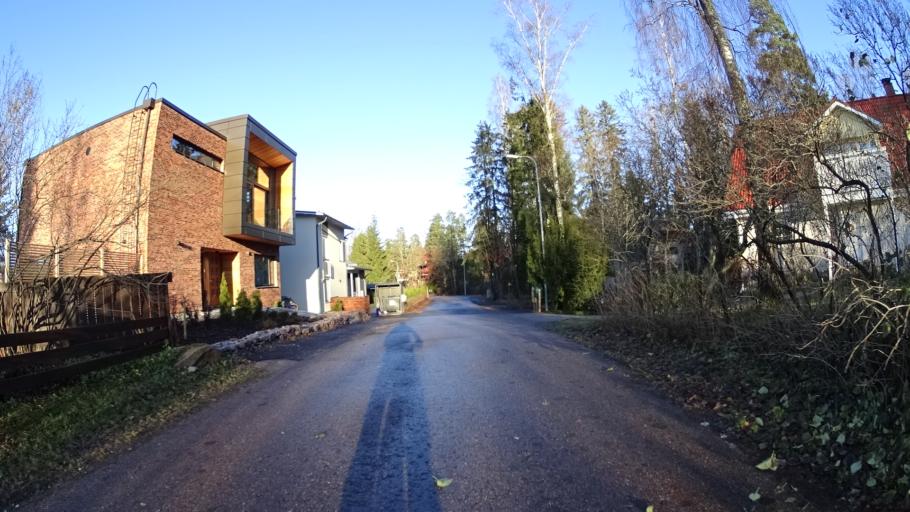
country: FI
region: Uusimaa
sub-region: Helsinki
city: Kauniainen
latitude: 60.2107
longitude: 24.7378
